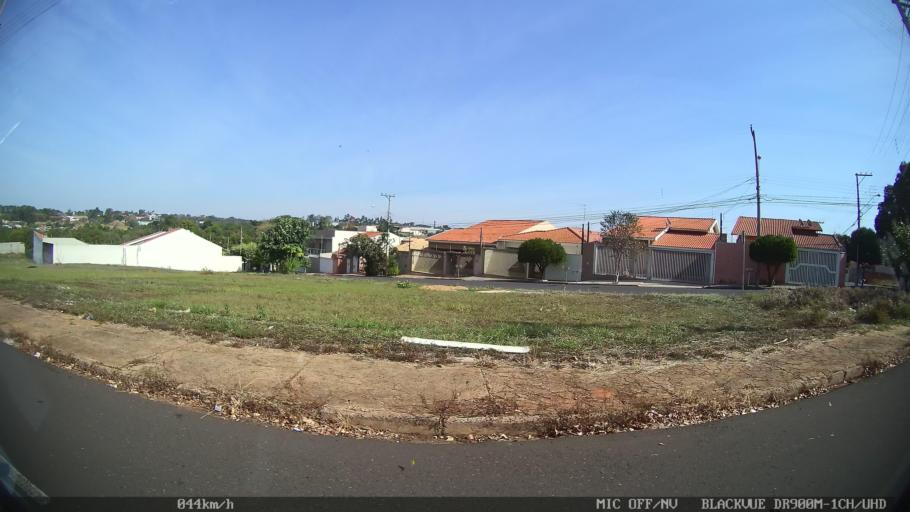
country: BR
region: Sao Paulo
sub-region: Sao Jose Do Rio Preto
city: Sao Jose do Rio Preto
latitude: -20.8015
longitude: -49.4153
